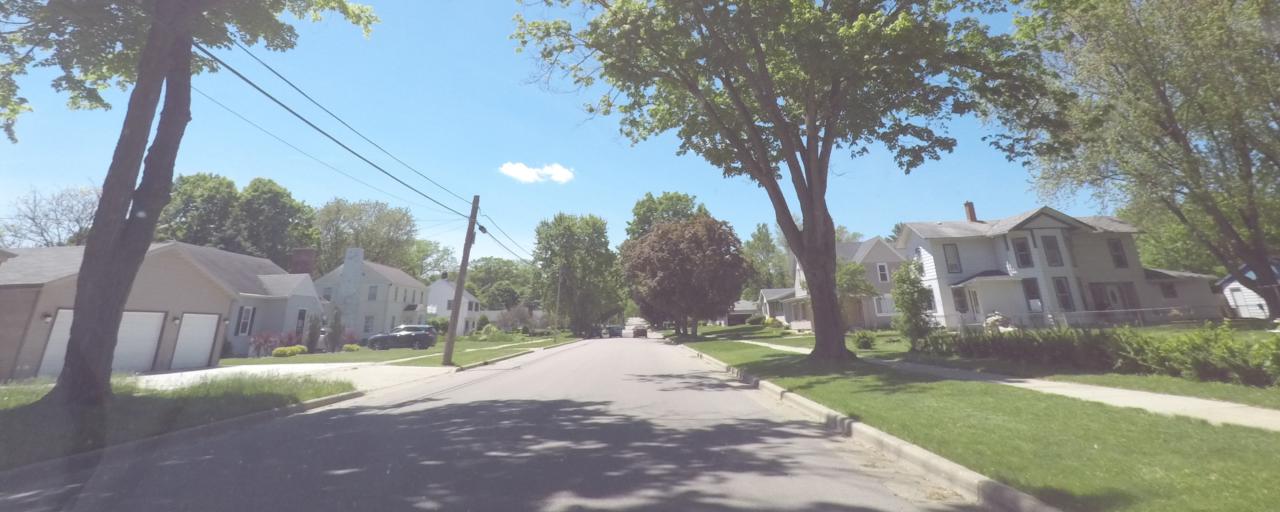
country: US
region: Wisconsin
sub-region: Rock County
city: Evansville
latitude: 42.7822
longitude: -89.3036
